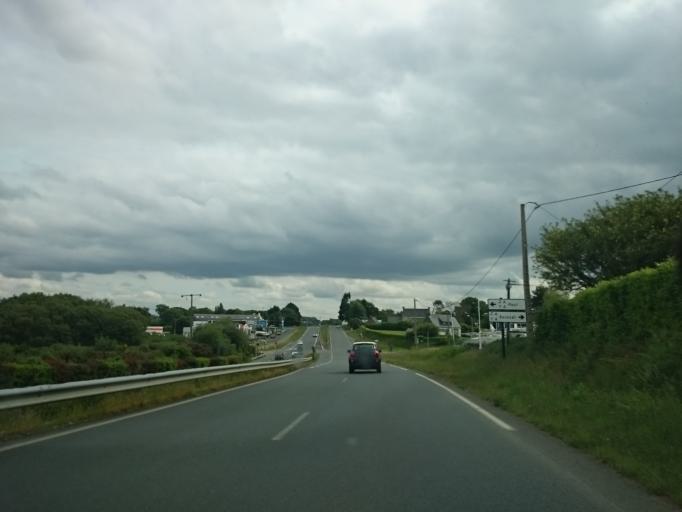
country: FR
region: Brittany
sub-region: Departement des Cotes-d'Armor
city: Saint-Quay-Perros
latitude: 48.7829
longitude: -3.4493
